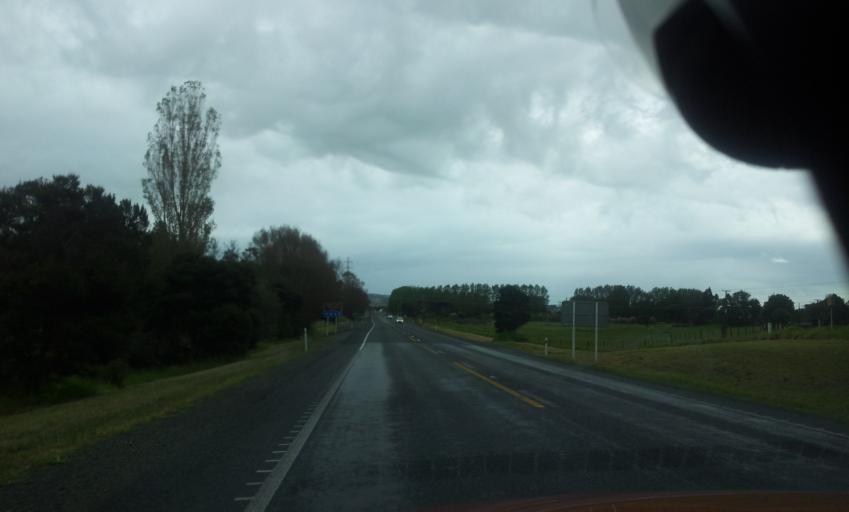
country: NZ
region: Northland
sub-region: Whangarei
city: Ruakaka
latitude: -35.9105
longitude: 174.4495
